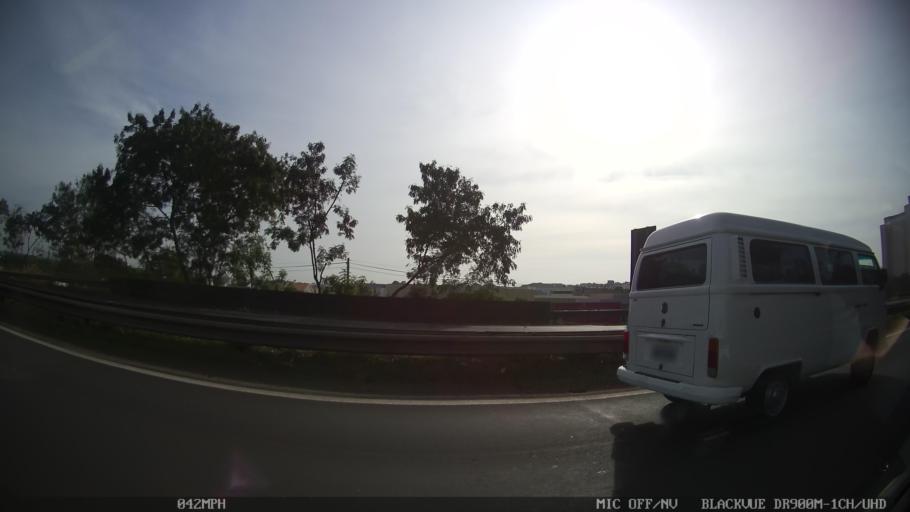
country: BR
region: Sao Paulo
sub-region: Piracicaba
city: Piracicaba
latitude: -22.6857
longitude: -47.6746
